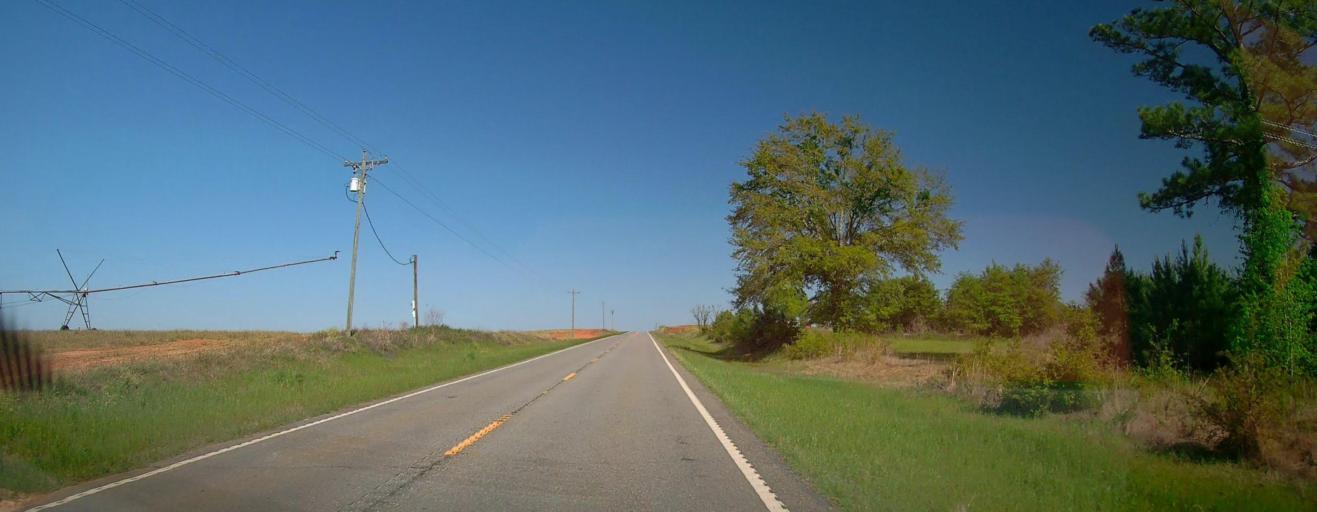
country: US
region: Georgia
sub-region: Dooly County
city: Unadilla
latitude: 32.2600
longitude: -83.6765
